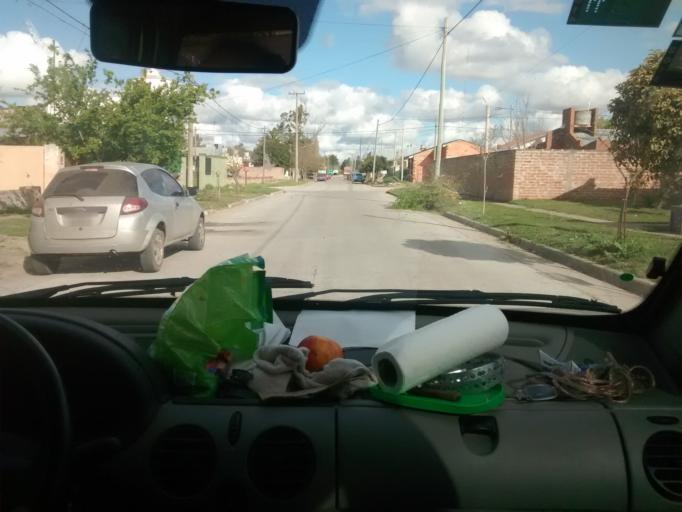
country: AR
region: Buenos Aires
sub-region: Partido de Loberia
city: Loberia
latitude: -38.1722
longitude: -58.7763
